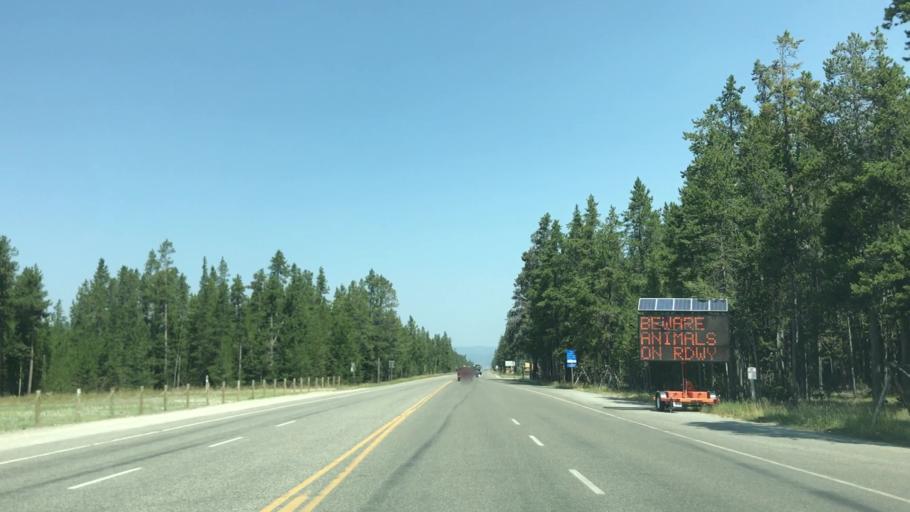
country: US
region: Montana
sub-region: Gallatin County
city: West Yellowstone
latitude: 44.6652
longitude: -111.0997
